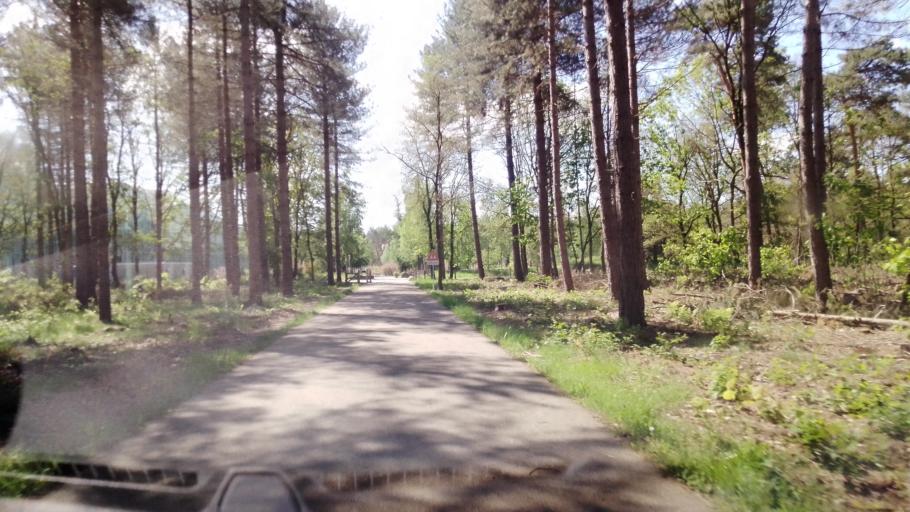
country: NL
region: Limburg
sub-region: Gemeente Venlo
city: Venlo
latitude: 51.4077
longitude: 6.1206
